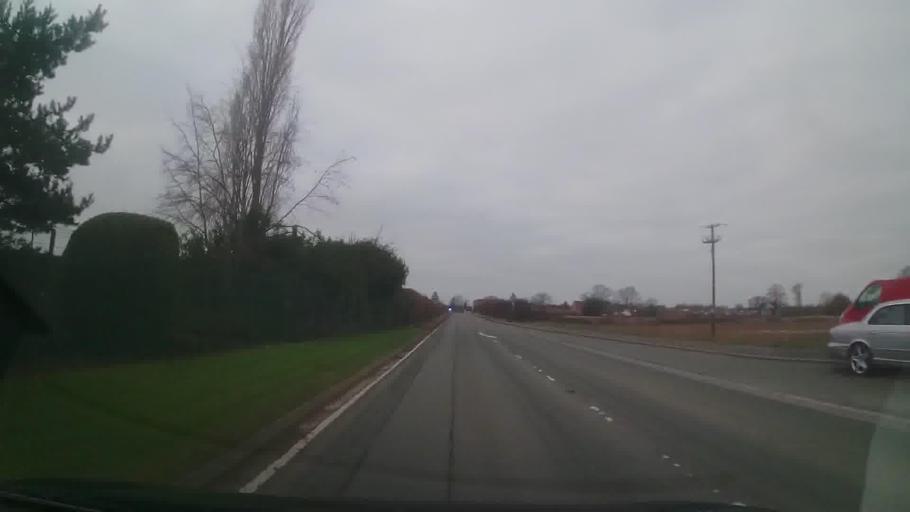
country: GB
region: England
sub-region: Shropshire
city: Bicton
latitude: 52.7238
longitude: -2.8101
